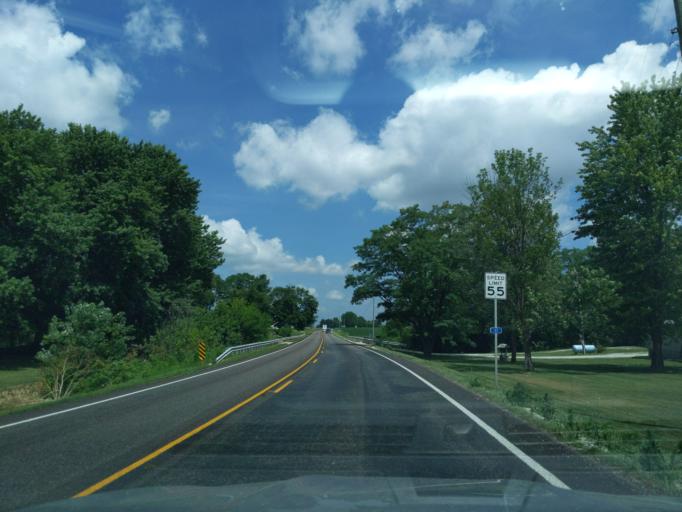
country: US
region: Indiana
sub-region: Ripley County
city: Osgood
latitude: 39.2075
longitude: -85.3306
